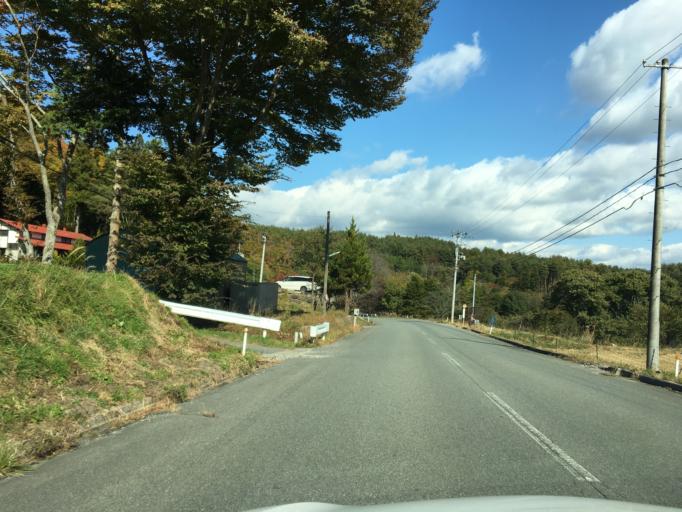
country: JP
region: Fukushima
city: Funehikimachi-funehiki
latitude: 37.3038
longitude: 140.7623
